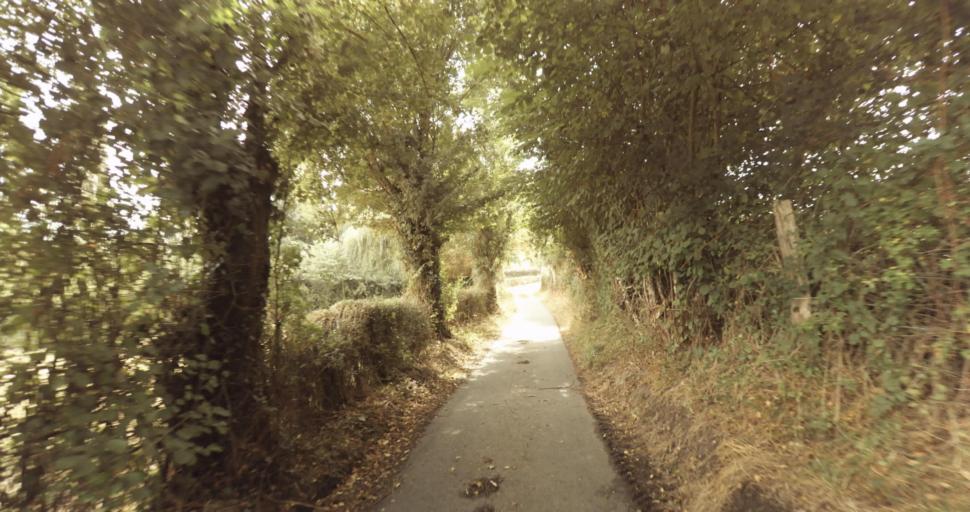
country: FR
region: Lower Normandy
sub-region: Departement de l'Orne
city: Gace
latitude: 48.8523
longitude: 0.2723
